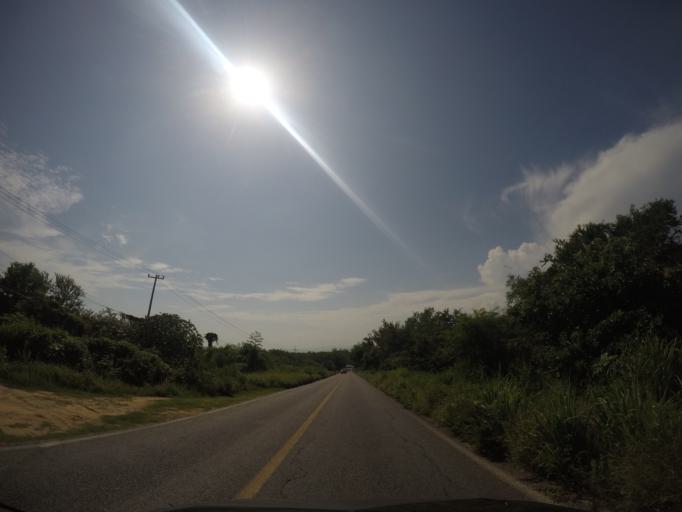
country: MX
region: Oaxaca
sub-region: San Pedro Mixtepec -Dto. 22 -
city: Puerto Escondido
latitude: 15.8778
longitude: -97.1024
